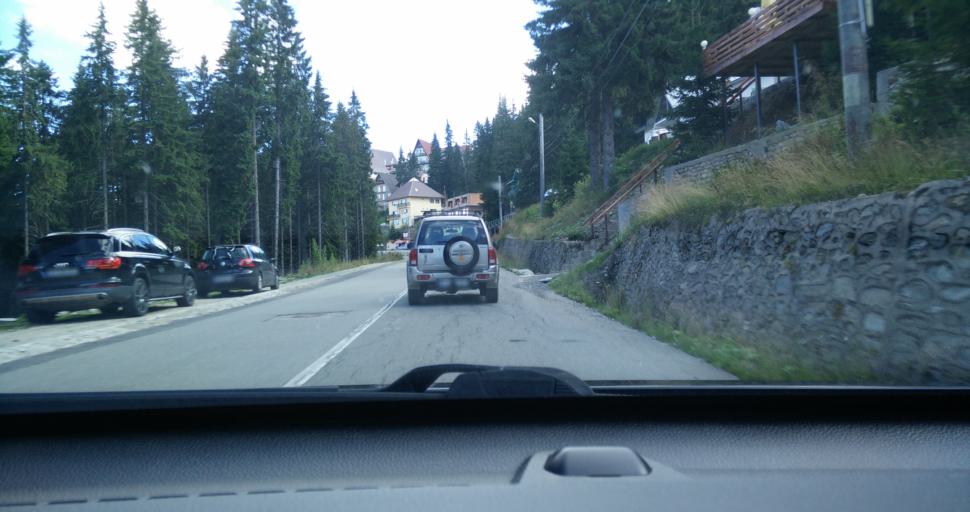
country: RO
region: Gorj
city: Novaci-Straini
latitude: 45.2854
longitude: 23.6917
